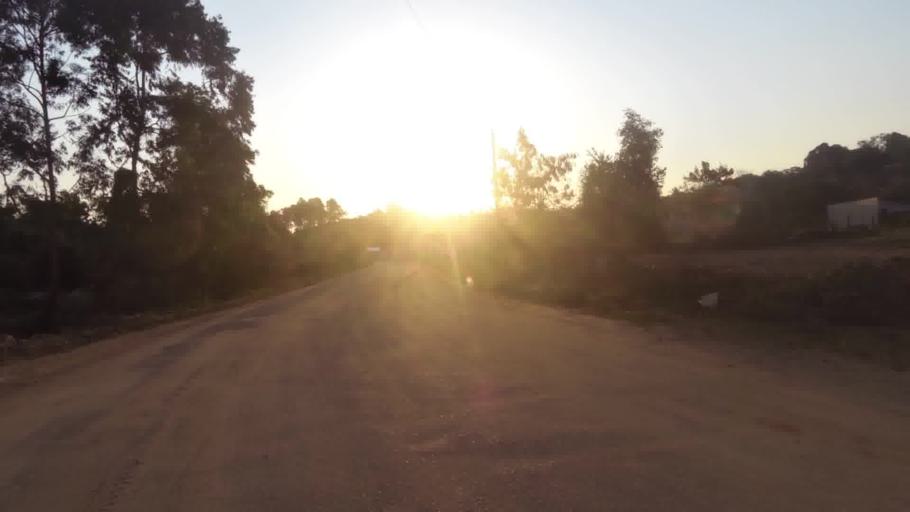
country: BR
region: Espirito Santo
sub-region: Piuma
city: Piuma
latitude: -20.8296
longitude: -40.7210
